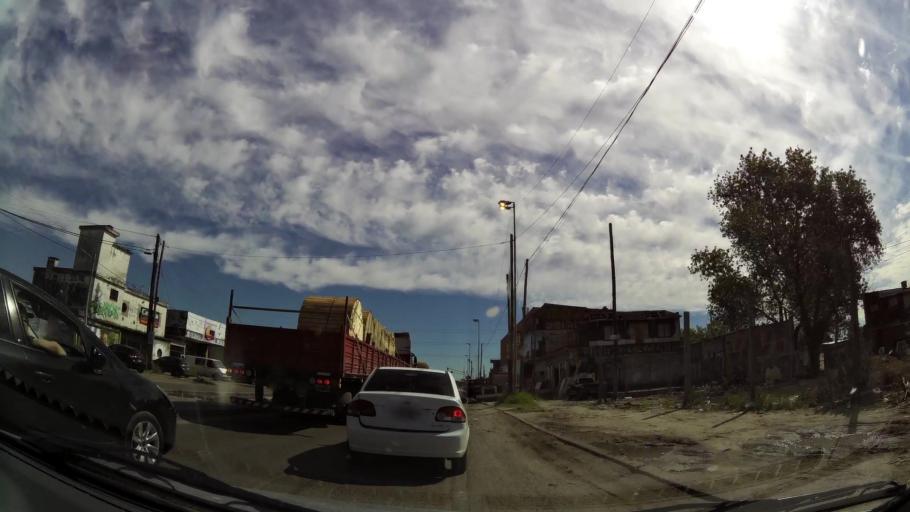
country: AR
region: Buenos Aires
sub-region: Partido de Almirante Brown
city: Adrogue
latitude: -34.7906
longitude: -58.3102
